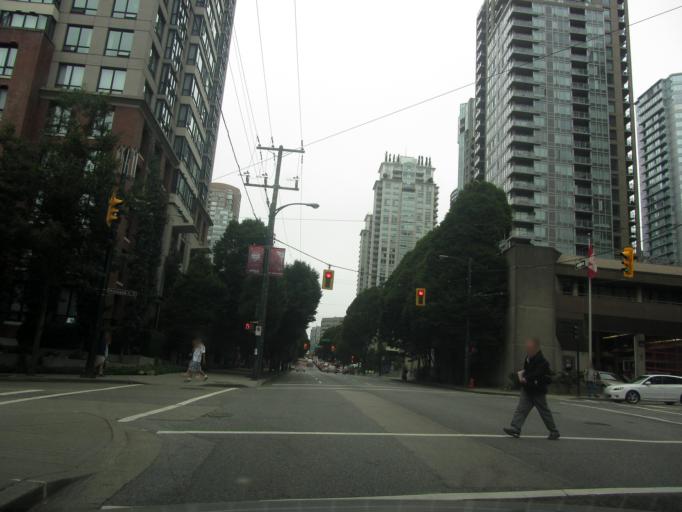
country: CA
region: British Columbia
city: West End
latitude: 49.2772
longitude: -123.1177
